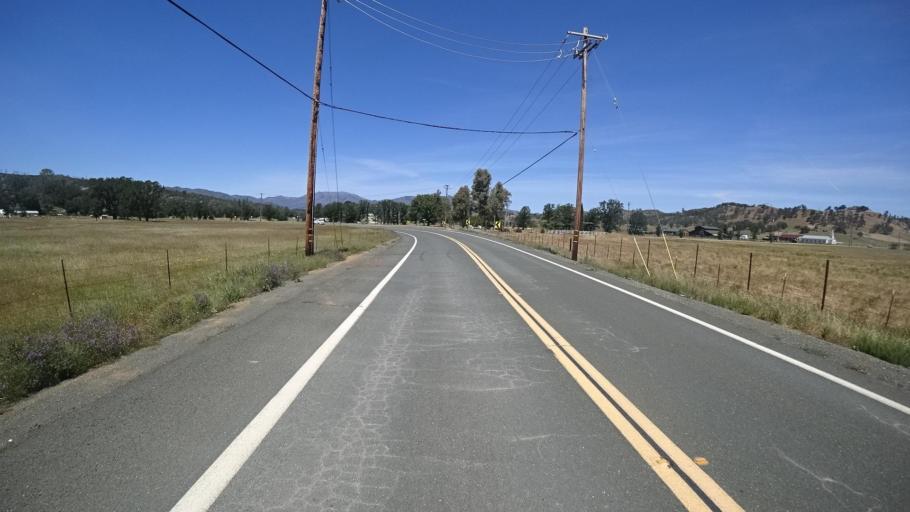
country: US
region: California
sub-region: Lake County
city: Middletown
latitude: 38.7460
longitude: -122.5781
